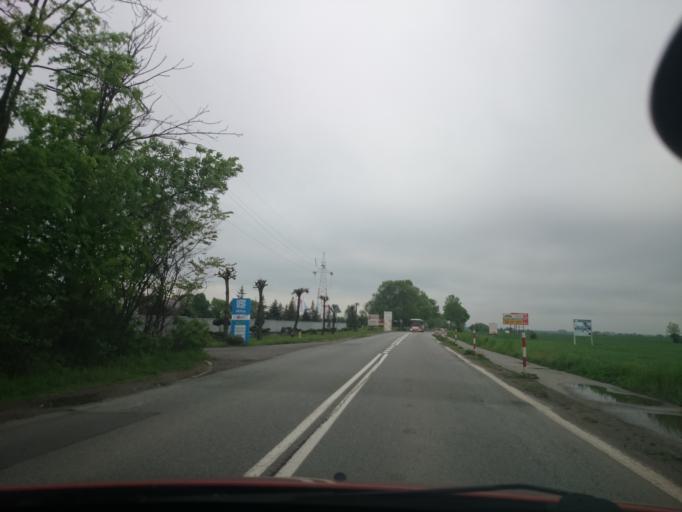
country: PL
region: Opole Voivodeship
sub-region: Powiat opolski
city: Opole
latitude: 50.6931
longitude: 17.9279
